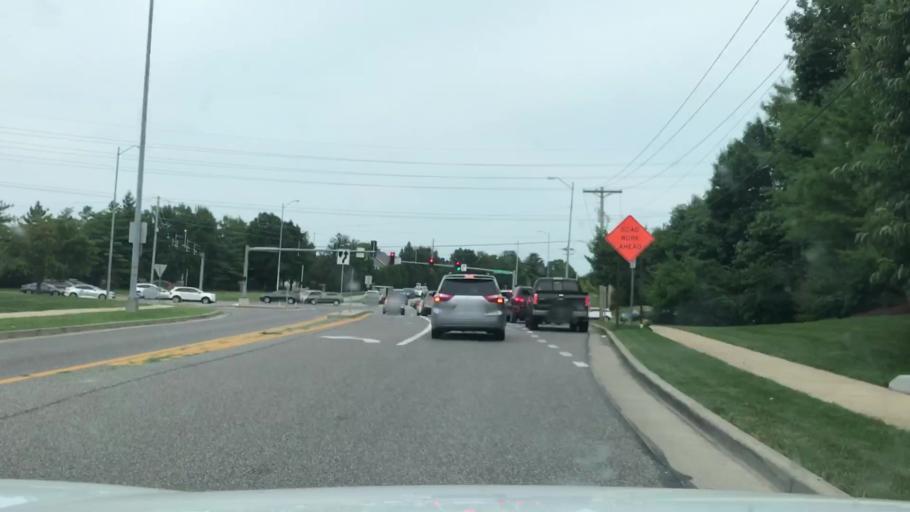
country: US
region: Missouri
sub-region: Saint Louis County
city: Clarkson Valley
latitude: 38.6220
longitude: -90.5831
